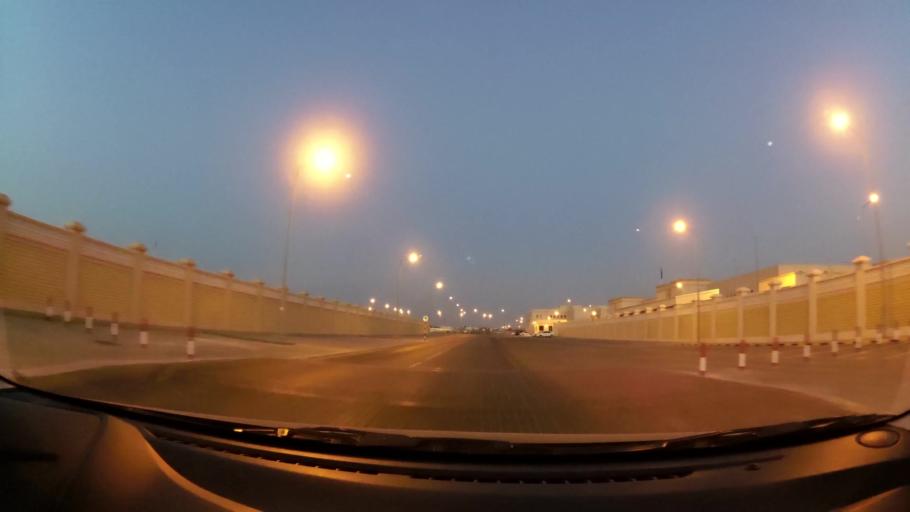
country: OM
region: Muhafazat Masqat
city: As Sib al Jadidah
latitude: 23.6634
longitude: 58.1873
